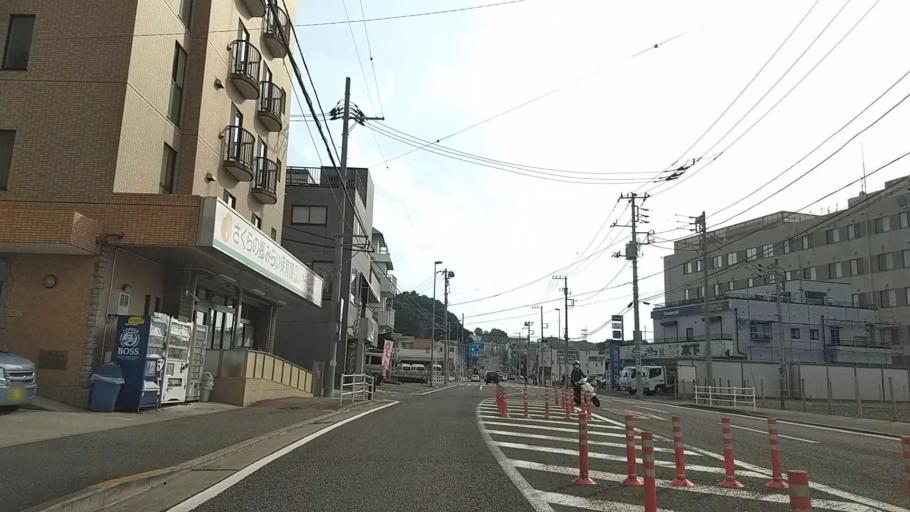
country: JP
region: Kanagawa
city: Yokohama
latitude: 35.5055
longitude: 139.5641
